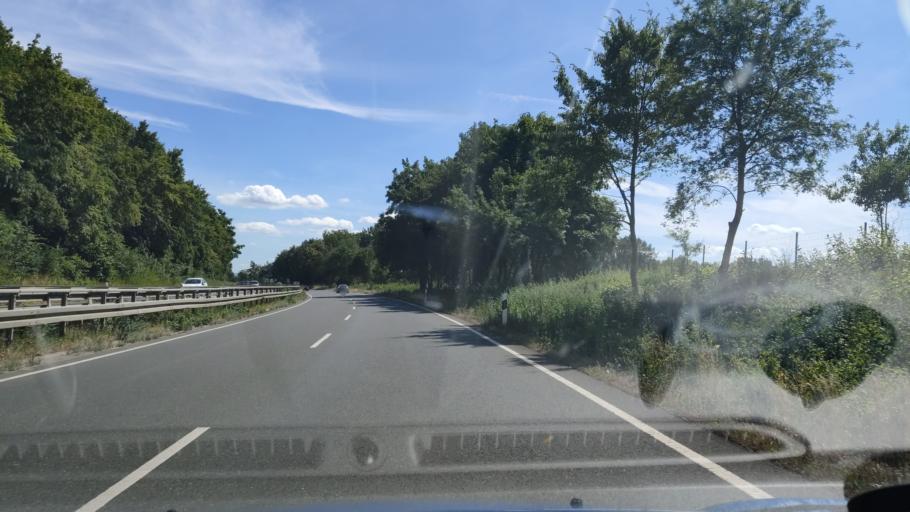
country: DE
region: Lower Saxony
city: Ronnenberg
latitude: 52.3458
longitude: 9.6424
